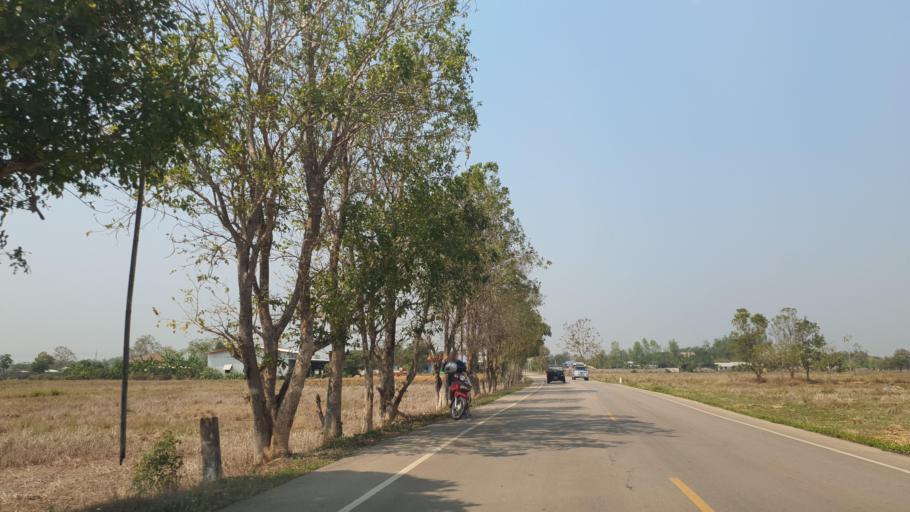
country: TH
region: Lamphun
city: Lamphun
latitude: 18.5506
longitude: 99.0801
